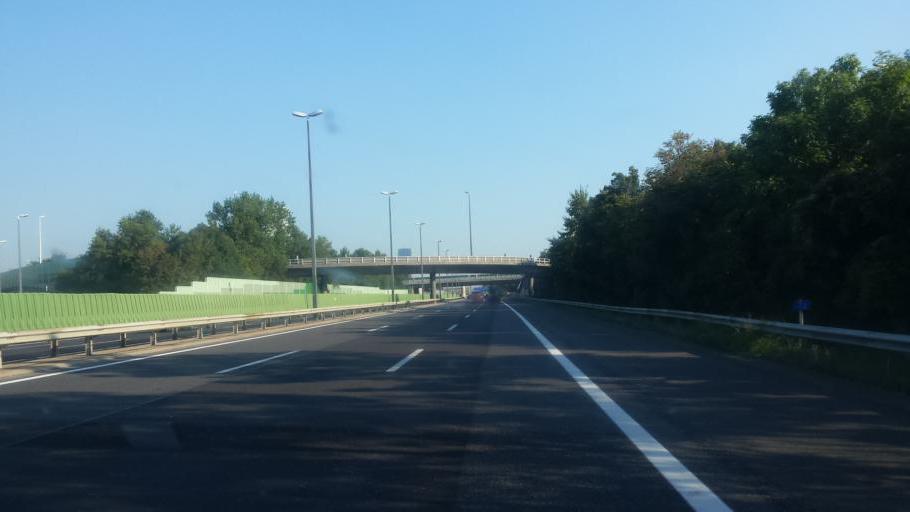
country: AT
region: Vienna
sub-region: Wien Stadt
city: Vienna
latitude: 48.2595
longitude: 16.3829
